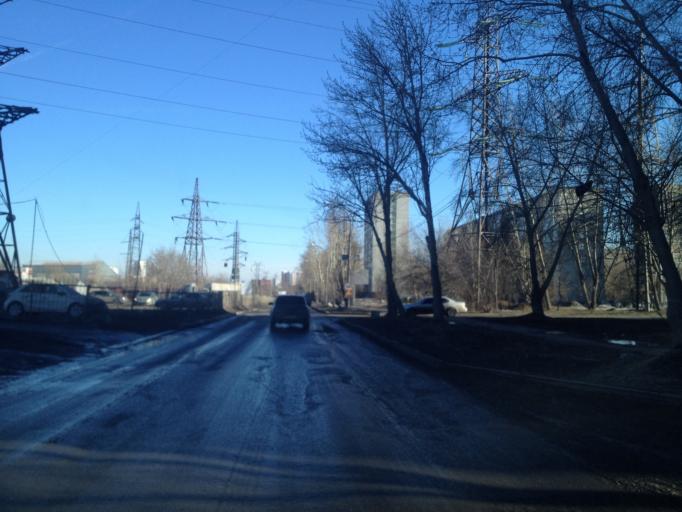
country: RU
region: Sverdlovsk
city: Yekaterinburg
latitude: 56.8732
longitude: 60.5582
